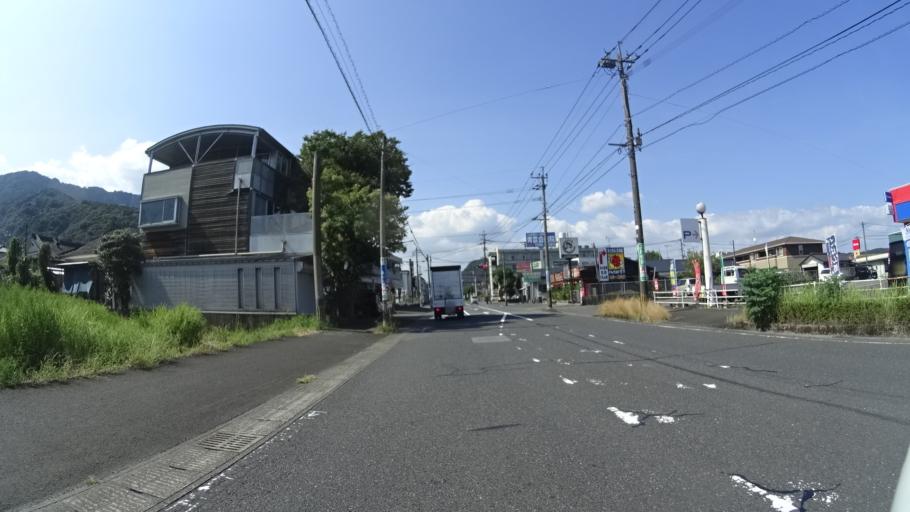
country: JP
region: Kagoshima
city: Kajiki
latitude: 31.7114
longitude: 130.6015
